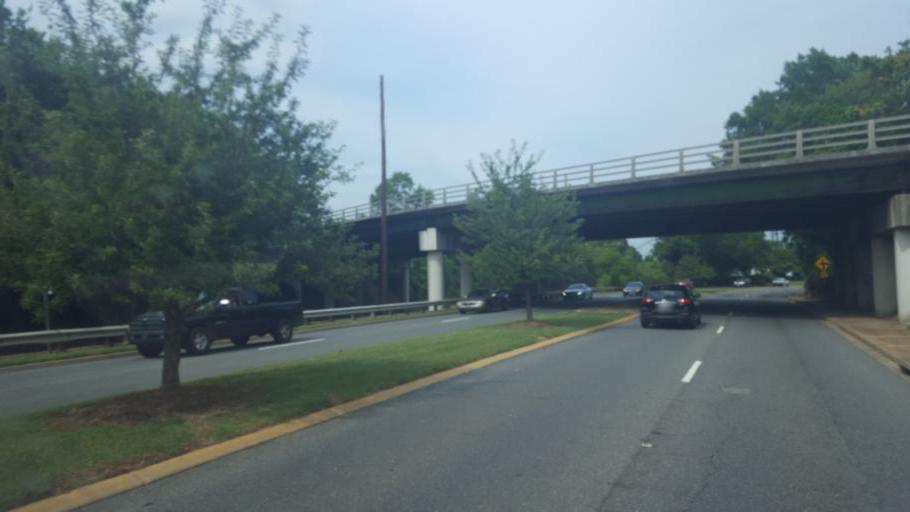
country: US
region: South Carolina
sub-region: York County
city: Rock Hill
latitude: 34.9293
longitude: -81.0233
